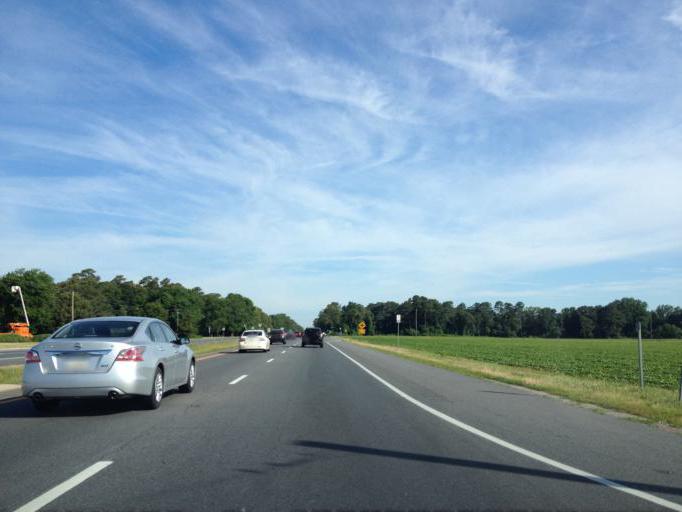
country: US
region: Delaware
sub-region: Sussex County
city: Millsboro
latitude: 38.5993
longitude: -75.3174
